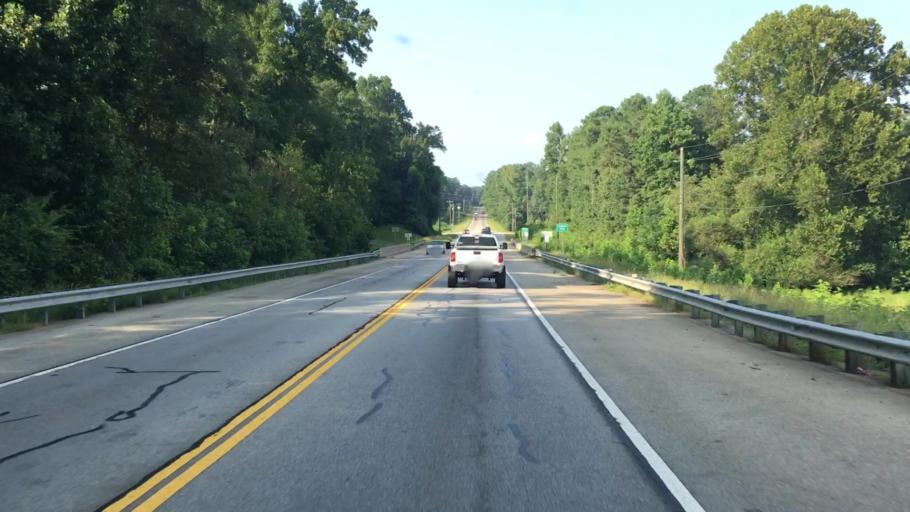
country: US
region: Georgia
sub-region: Barrow County
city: Russell
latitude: 33.9579
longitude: -83.7204
